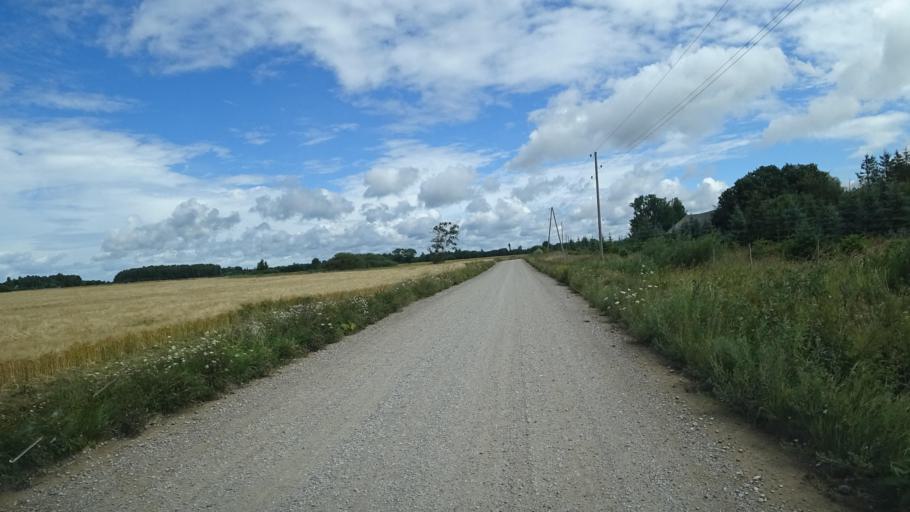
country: LV
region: Liepaja
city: Vec-Liepaja
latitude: 56.6547
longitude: 21.0564
